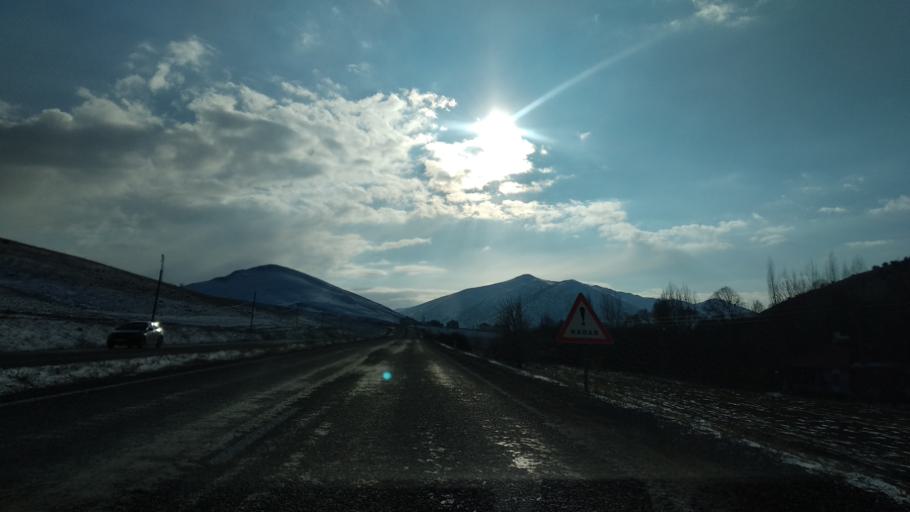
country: TR
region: Kayseri
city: Sariz
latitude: 38.3593
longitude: 36.4394
